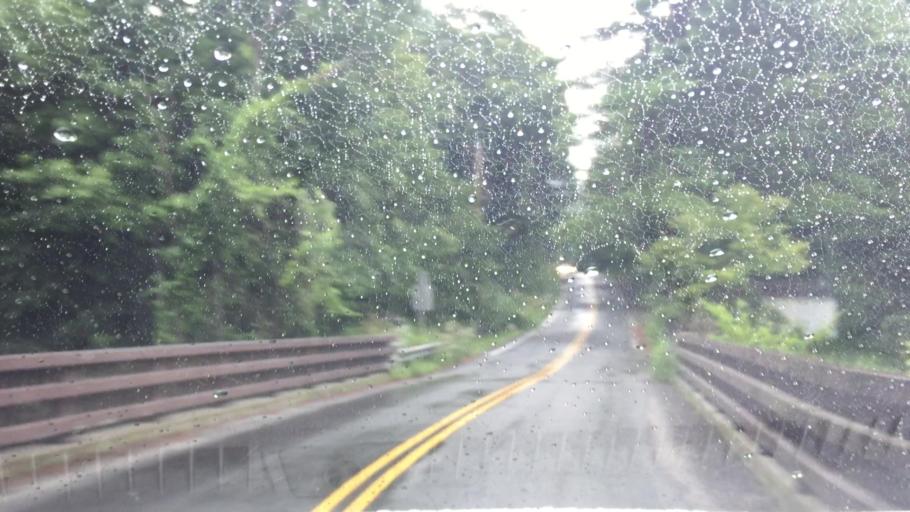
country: US
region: Massachusetts
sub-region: Berkshire County
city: West Stockbridge
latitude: 42.3025
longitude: -73.3807
